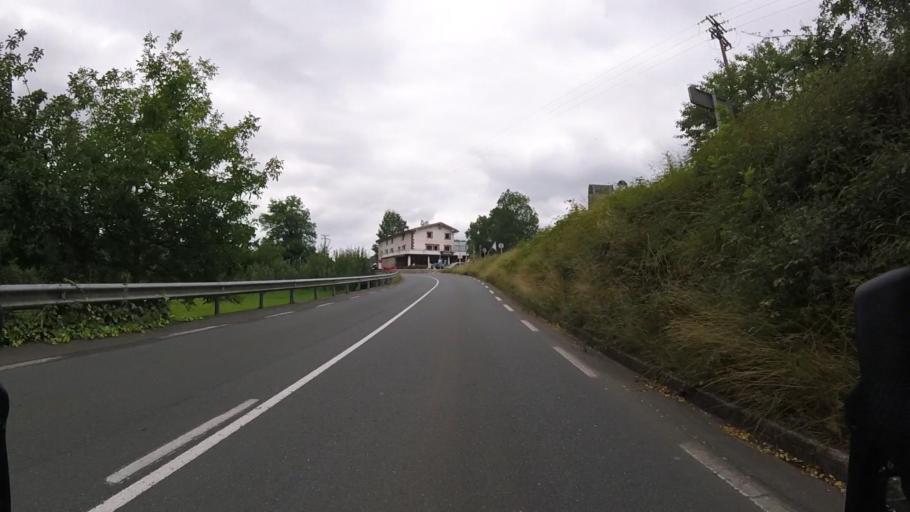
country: ES
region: Basque Country
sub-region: Provincia de Guipuzcoa
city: Lezo
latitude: 43.2918
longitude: -1.8441
